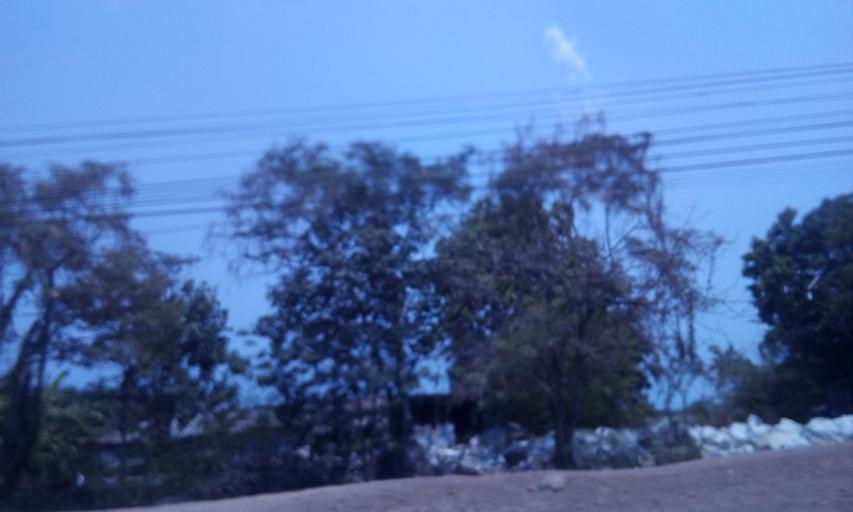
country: TH
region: Chachoengsao
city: Ban Pho
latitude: 13.5912
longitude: 101.1211
